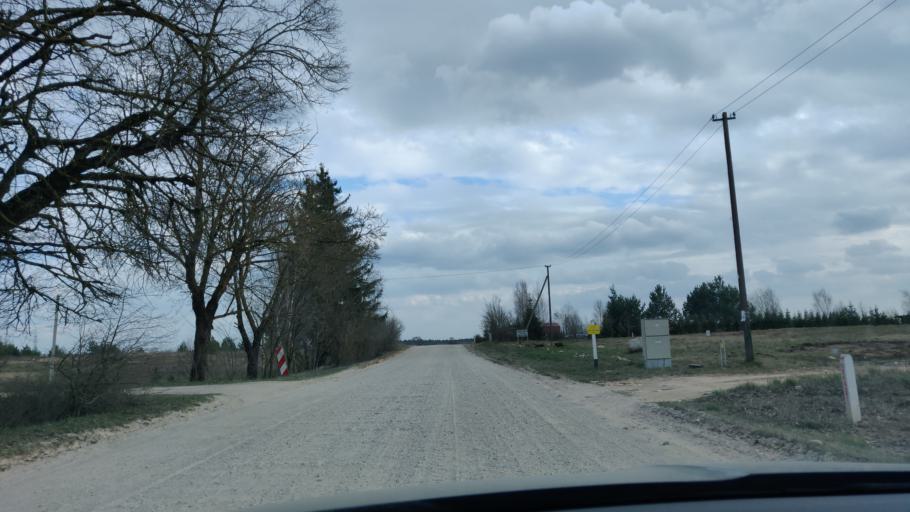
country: LT
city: Lentvaris
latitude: 54.6156
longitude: 25.0682
